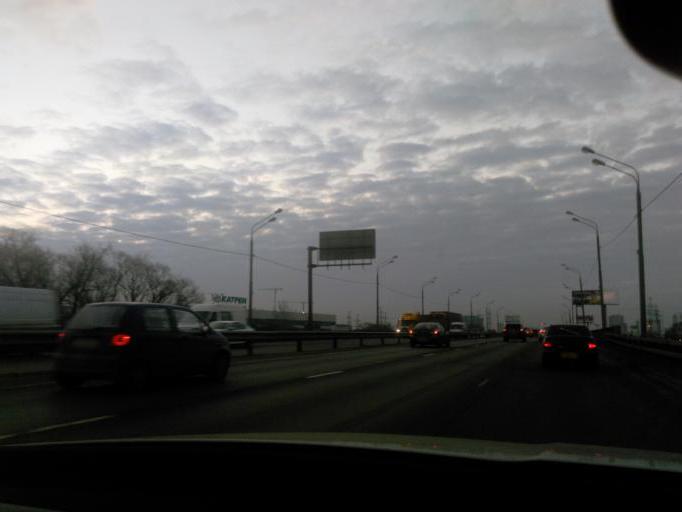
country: RU
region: Moscow
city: Khimki
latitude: 55.9190
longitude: 37.3949
